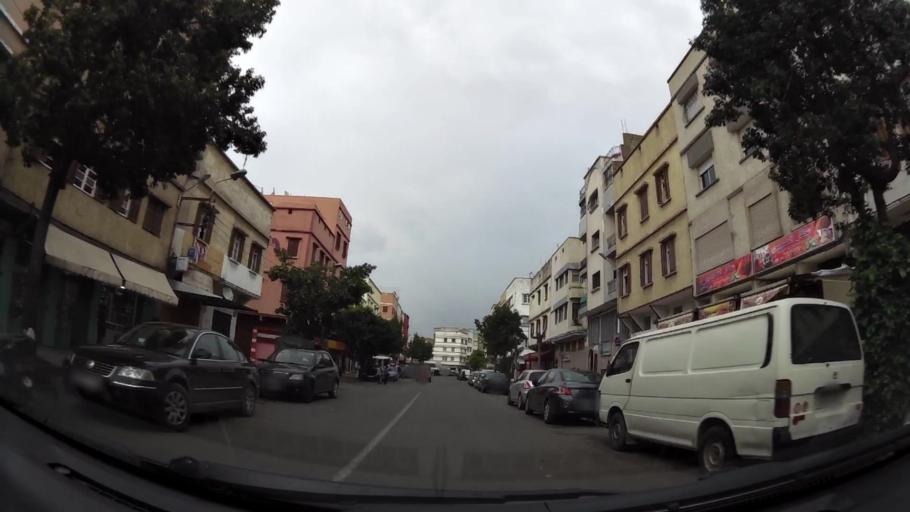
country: MA
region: Grand Casablanca
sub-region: Casablanca
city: Casablanca
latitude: 33.5565
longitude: -7.6038
